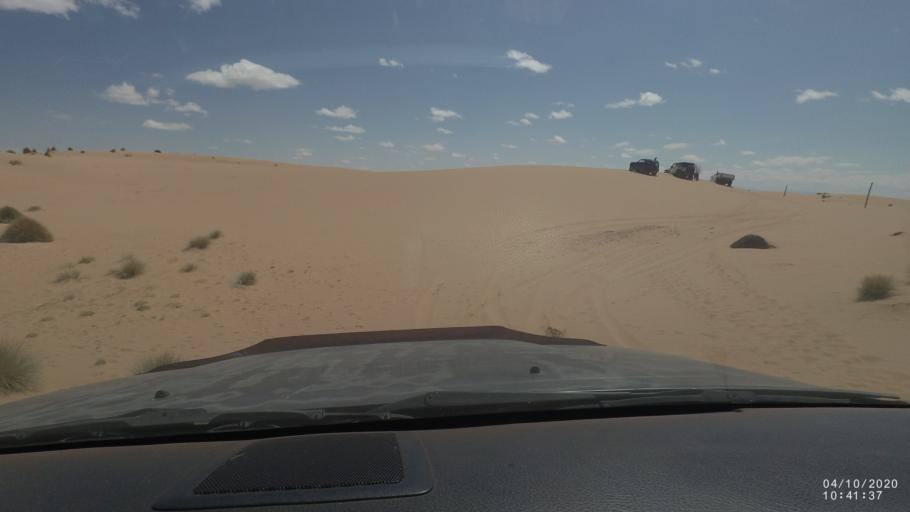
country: BO
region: Oruro
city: Poopo
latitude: -18.7045
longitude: -67.4717
